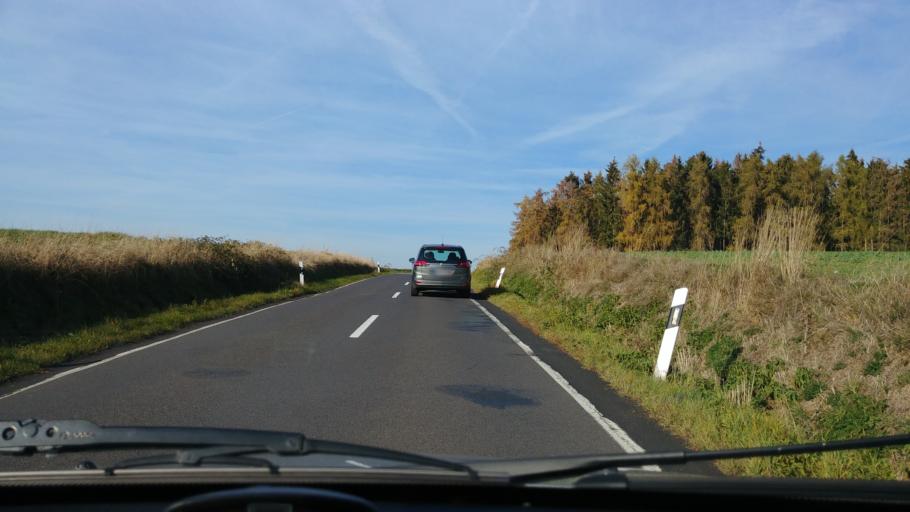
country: DE
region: Hesse
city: Burg Hohenstein
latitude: 50.2044
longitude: 8.0966
